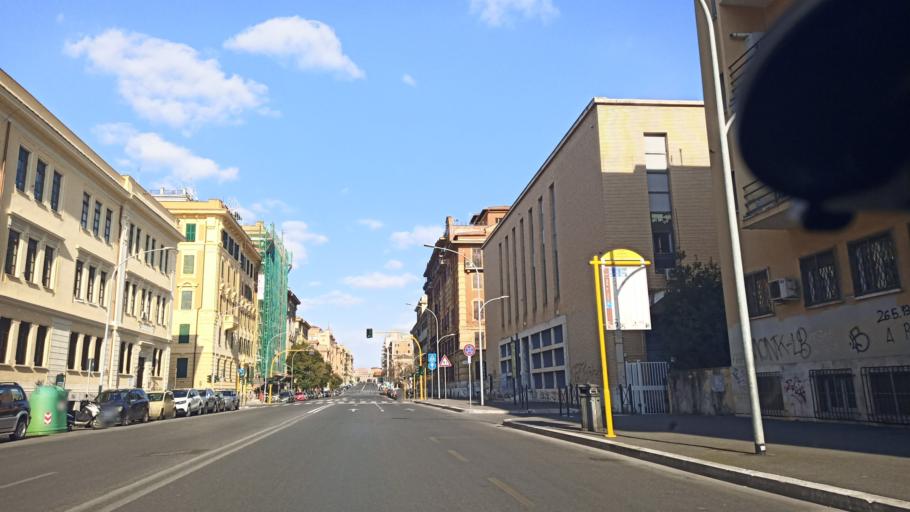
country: IT
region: Latium
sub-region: Citta metropolitana di Roma Capitale
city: Rome
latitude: 41.8857
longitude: 12.5118
